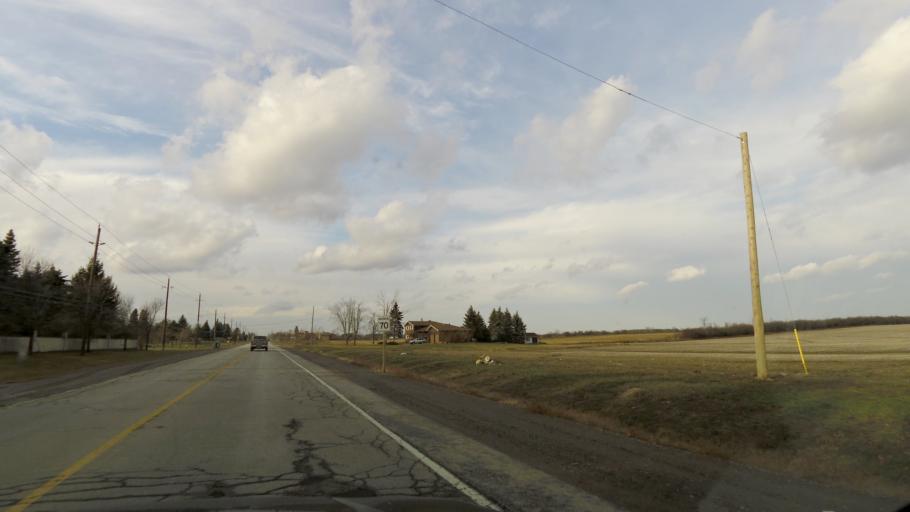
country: CA
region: Ontario
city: Brampton
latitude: 43.8028
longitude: -79.7047
